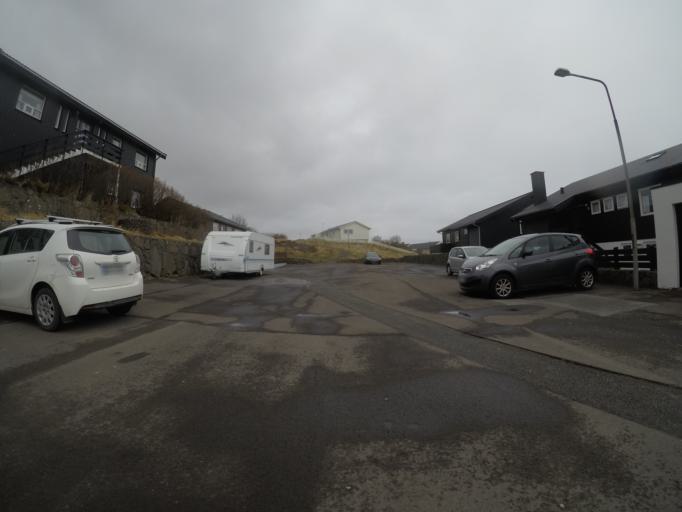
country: FO
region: Streymoy
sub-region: Torshavn
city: Torshavn
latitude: 62.0156
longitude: -6.7690
